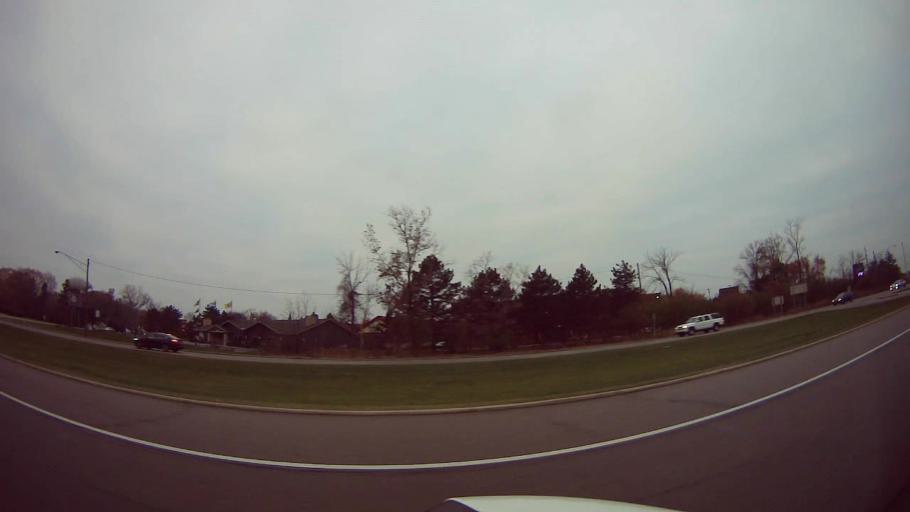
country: US
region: Michigan
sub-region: Oakland County
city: Clawson
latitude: 42.5568
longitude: -83.1282
